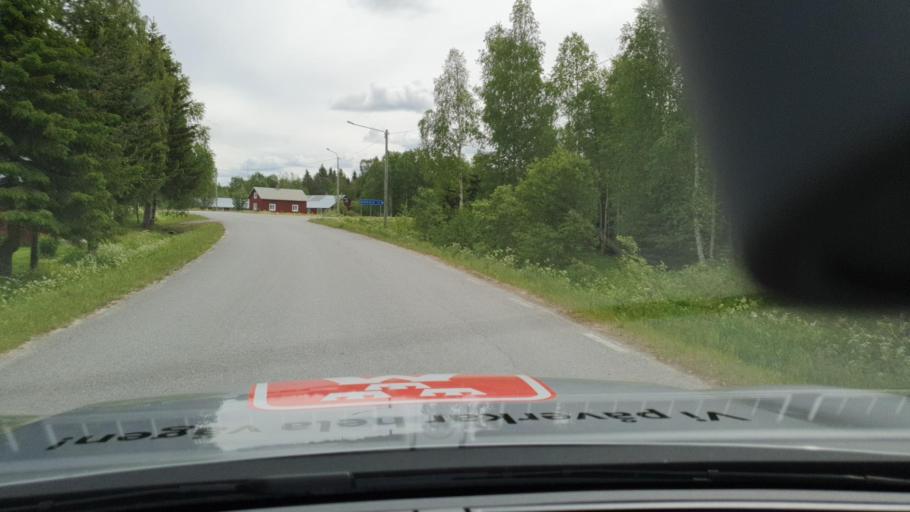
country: SE
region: Norrbotten
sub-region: Haparanda Kommun
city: Haparanda
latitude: 65.9479
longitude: 23.7963
